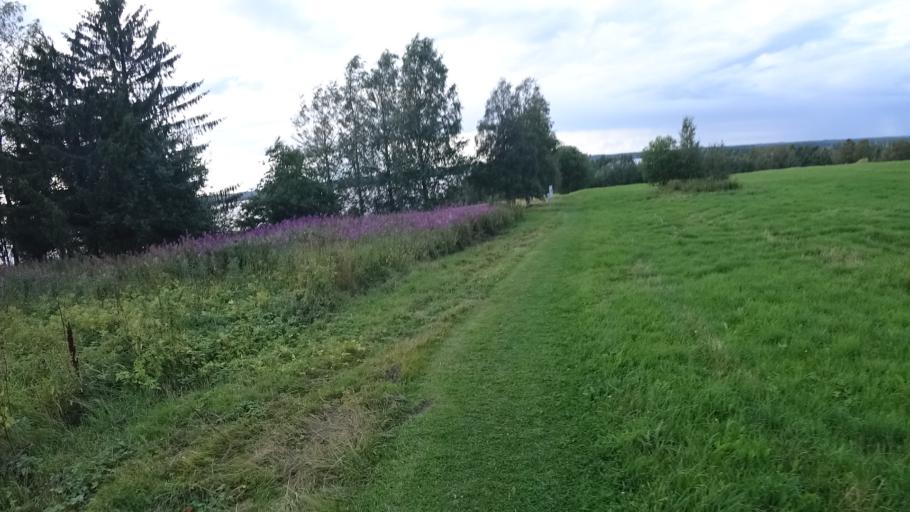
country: FI
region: North Karelia
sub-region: Joensuu
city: Ilomantsi
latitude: 62.6726
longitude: 30.9185
